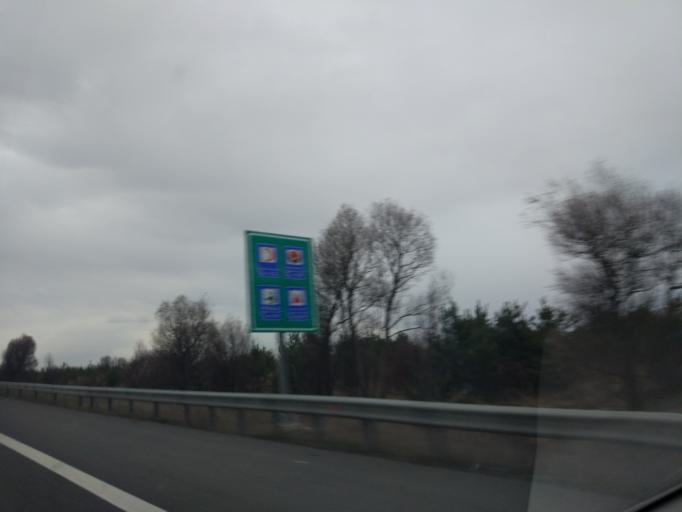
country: TR
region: Bolu
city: Gerede
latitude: 40.7401
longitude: 32.1756
